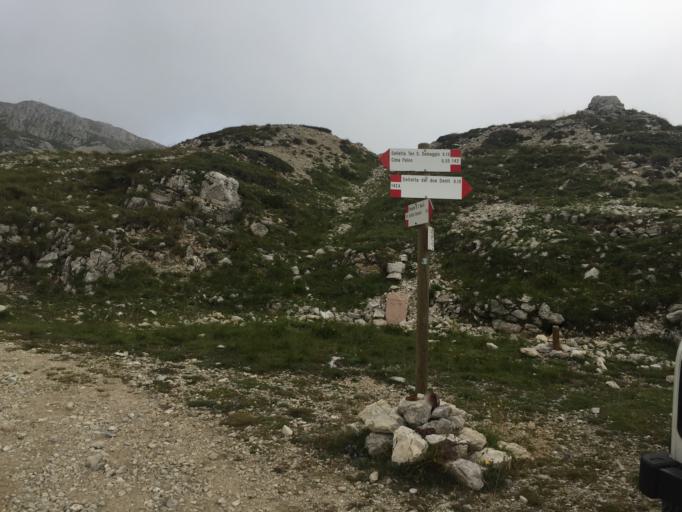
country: IT
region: Trentino-Alto Adige
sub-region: Provincia di Trento
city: Vallarsa
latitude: 45.7936
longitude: 11.1802
